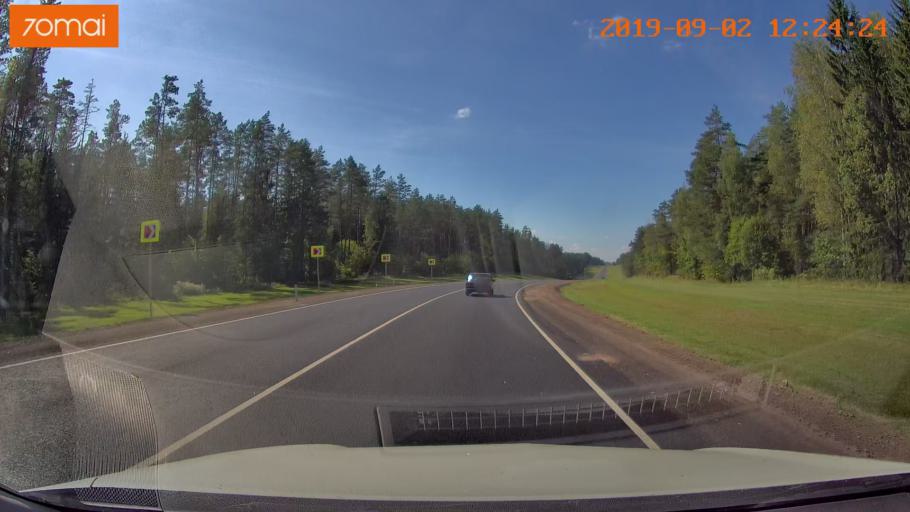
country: RU
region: Smolensk
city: Shumyachi
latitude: 53.8685
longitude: 32.6088
